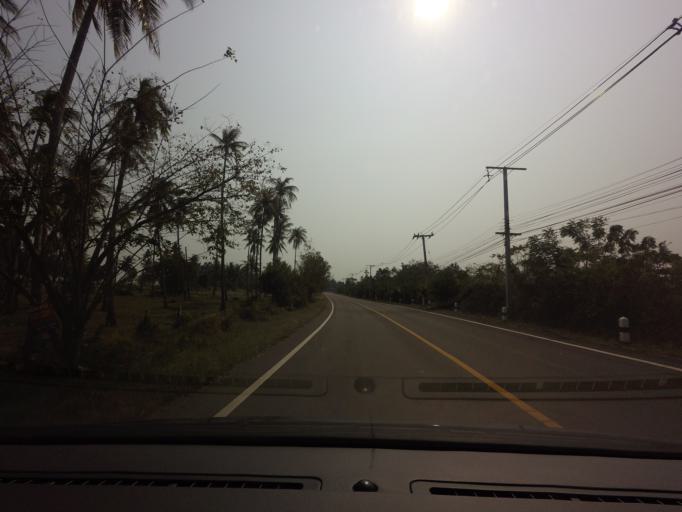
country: TH
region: Prachuap Khiri Khan
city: Kui Buri
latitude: 12.0307
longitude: 99.8953
